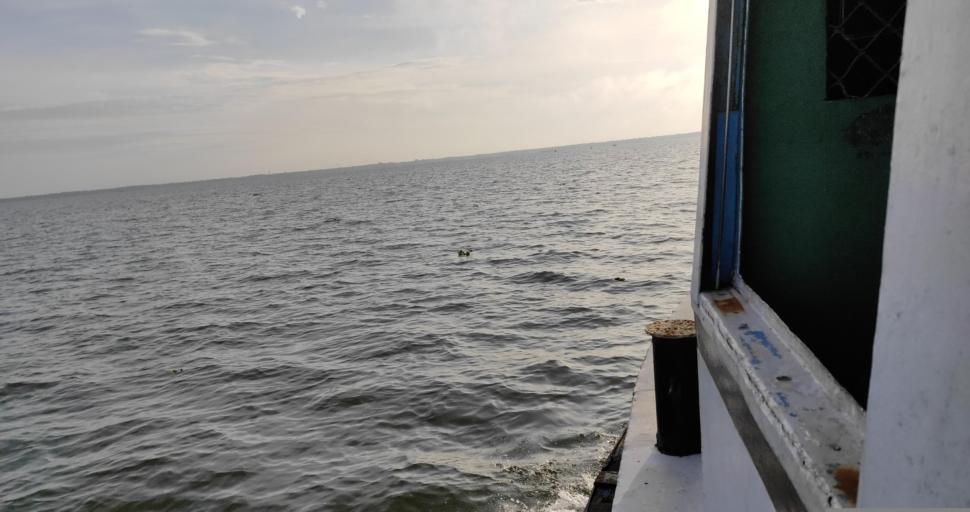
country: IN
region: Kerala
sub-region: Alappuzha
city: Shertallai
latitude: 9.6023
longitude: 76.3916
